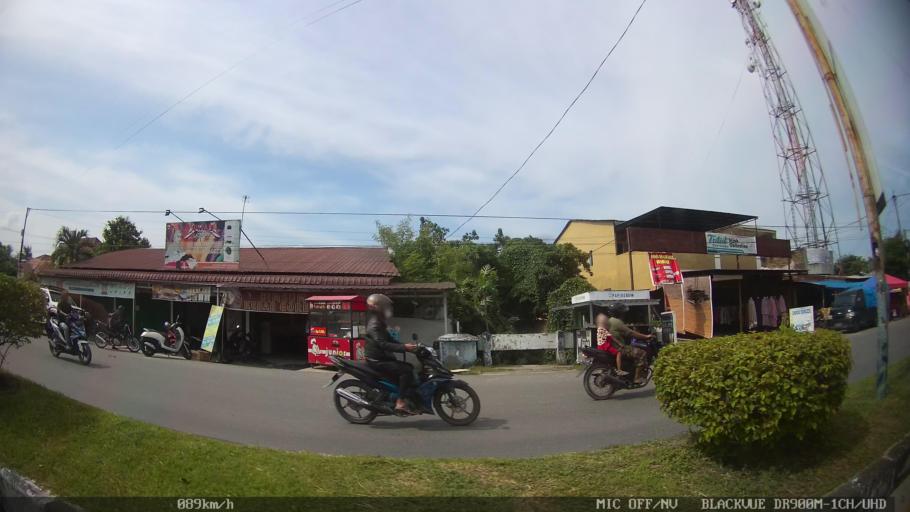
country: ID
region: North Sumatra
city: Percut
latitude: 3.6123
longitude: 98.8053
